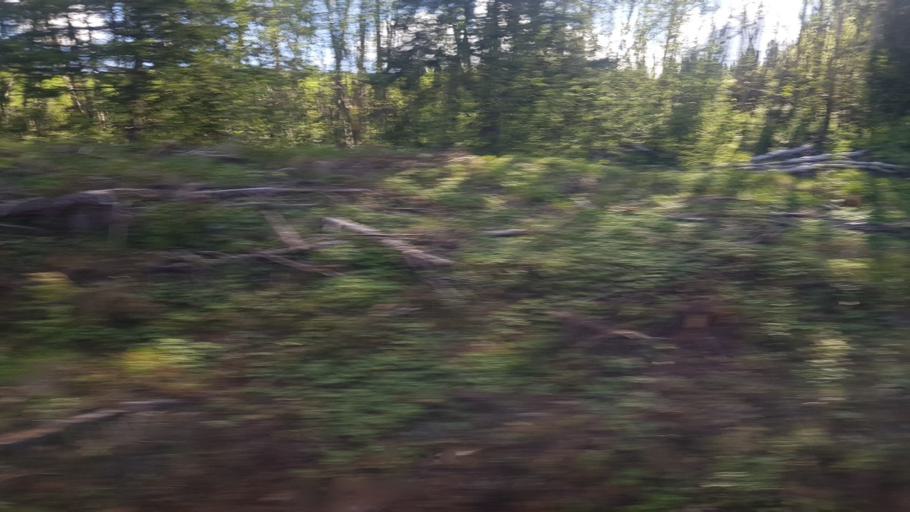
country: NO
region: Sor-Trondelag
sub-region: Rennebu
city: Berkak
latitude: 62.8493
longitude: 10.0214
